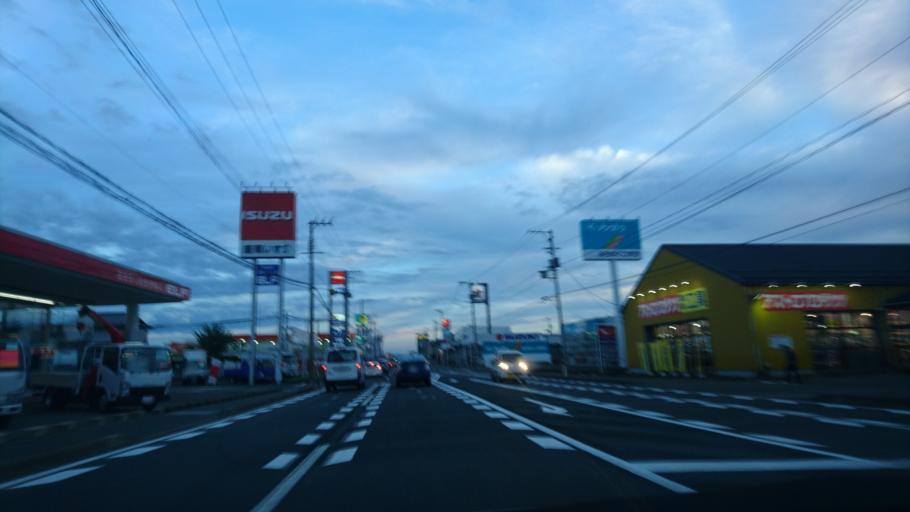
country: JP
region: Iwate
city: Morioka-shi
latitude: 39.6670
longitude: 141.1580
